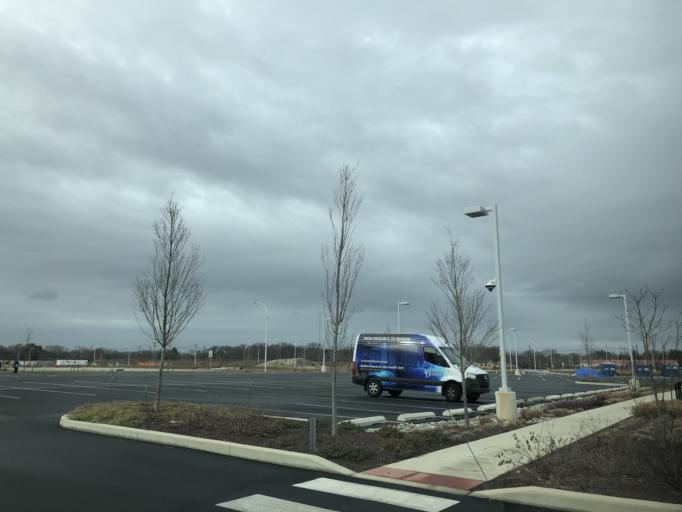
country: US
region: Delaware
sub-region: New Castle County
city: Newark
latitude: 39.6641
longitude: -75.7548
